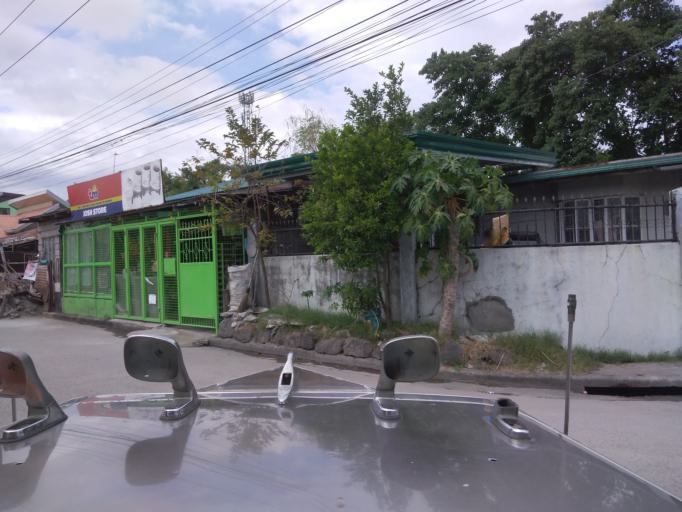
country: PH
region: Central Luzon
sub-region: Province of Pampanga
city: Pandacaqui
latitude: 15.1794
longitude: 120.6505
